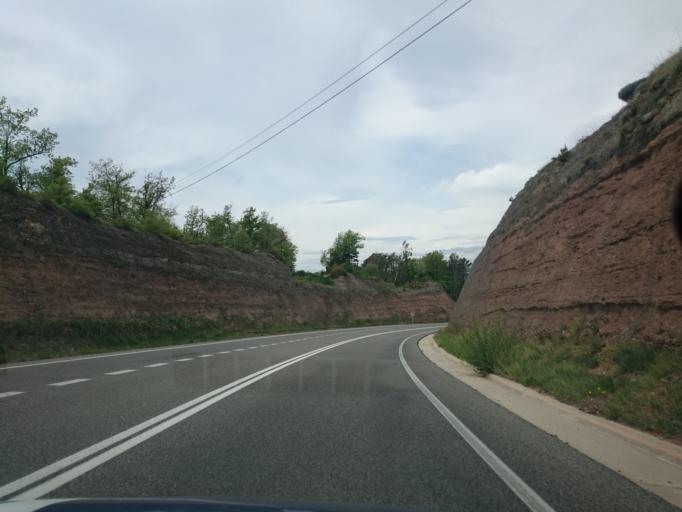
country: ES
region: Catalonia
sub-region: Provincia de Barcelona
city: Olost
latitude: 41.9730
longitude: 2.1195
